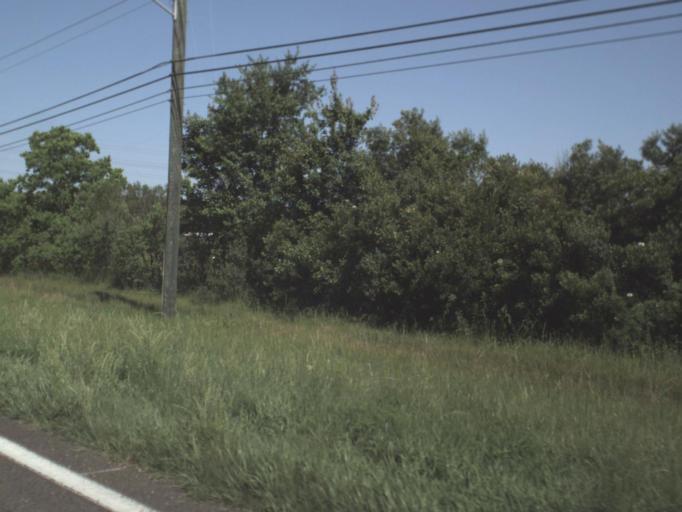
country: US
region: Florida
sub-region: Duval County
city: Baldwin
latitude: 30.3038
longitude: -81.9472
